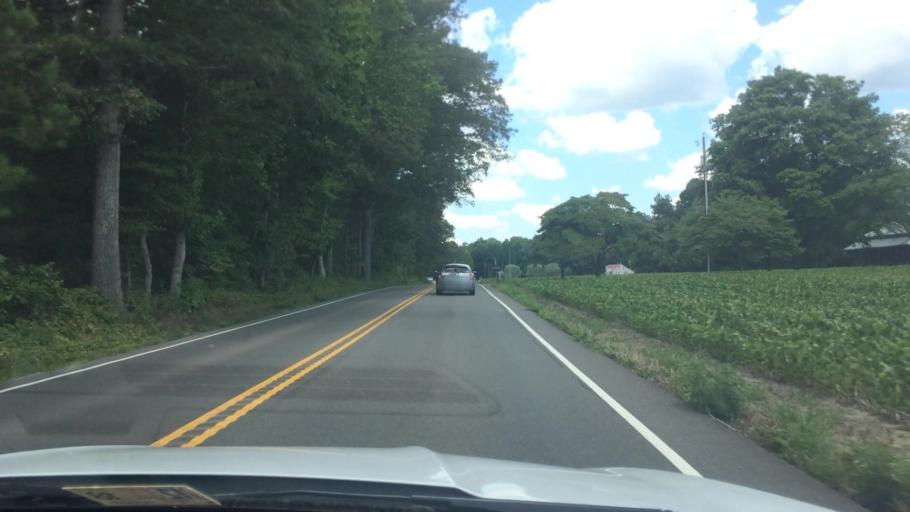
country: US
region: Virginia
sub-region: King William County
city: West Point
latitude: 37.6010
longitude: -76.7681
